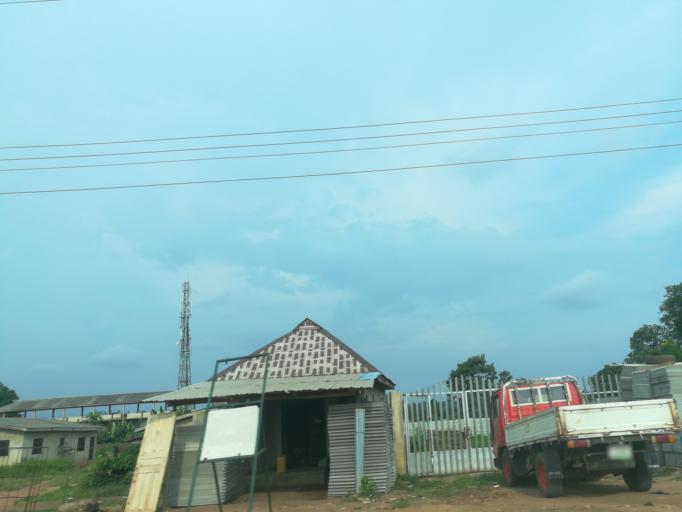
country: NG
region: Lagos
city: Ikorodu
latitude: 6.6568
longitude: 3.6691
